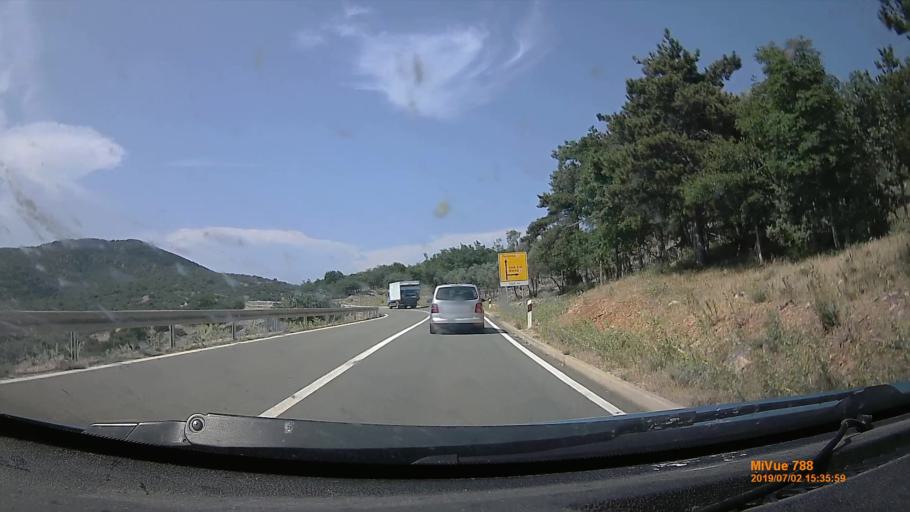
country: HR
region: Primorsko-Goranska
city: Cres
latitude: 44.9813
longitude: 14.4112
